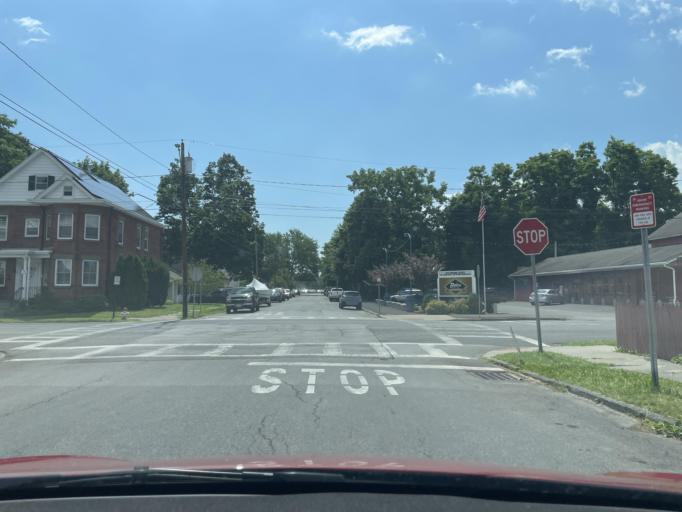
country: US
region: New York
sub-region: Ulster County
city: Kingston
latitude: 41.9321
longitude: -74.0038
